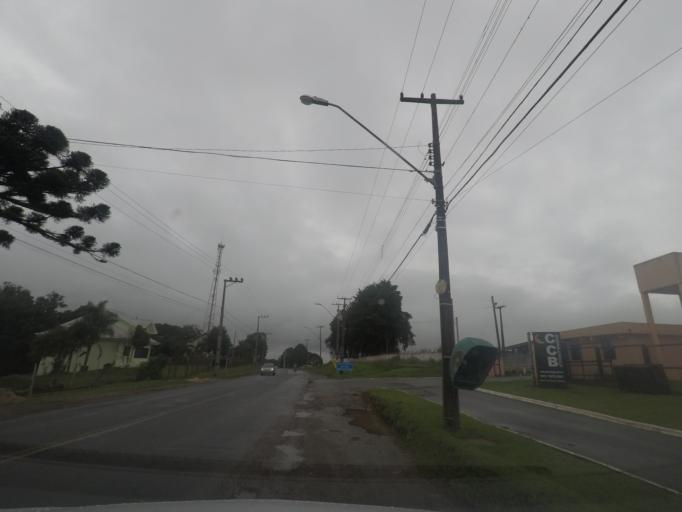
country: BR
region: Parana
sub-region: Quatro Barras
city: Quatro Barras
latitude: -25.3412
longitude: -49.0820
